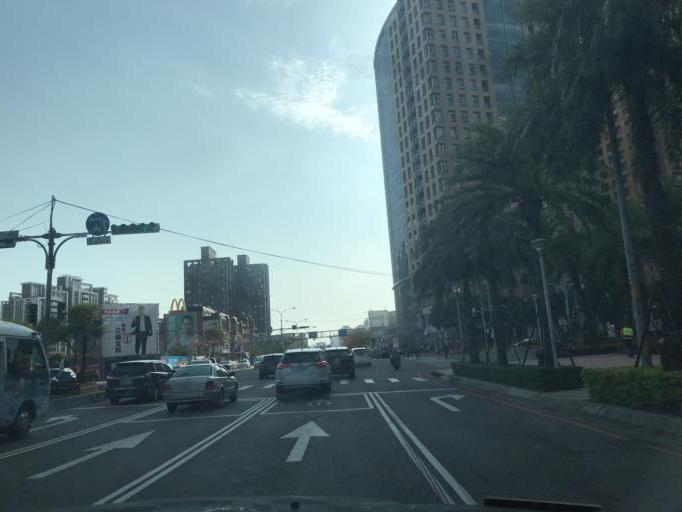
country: TW
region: Taiwan
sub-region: Hsinchu
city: Zhubei
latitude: 24.8203
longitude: 121.0285
